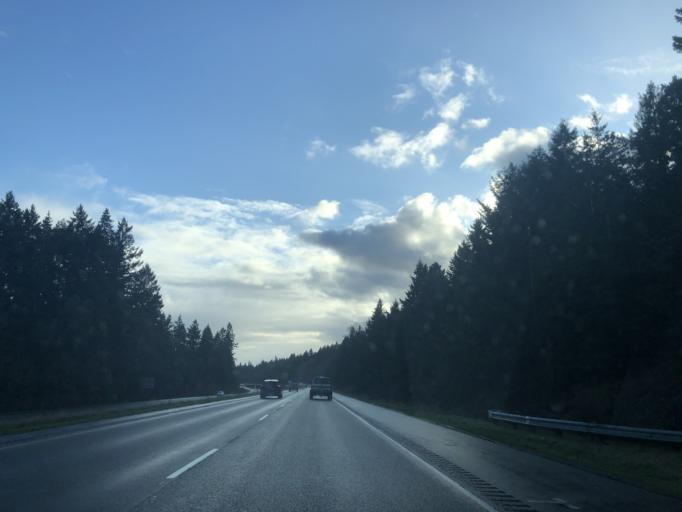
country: US
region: Washington
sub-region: Kitsap County
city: Chico
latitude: 47.6152
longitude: -122.7124
